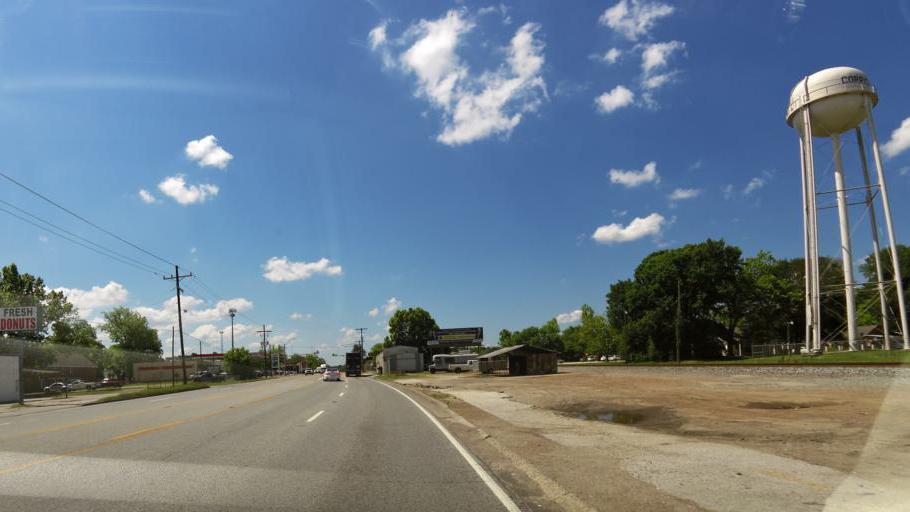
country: US
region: Texas
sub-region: Polk County
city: Corrigan
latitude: 30.9984
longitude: -94.8273
